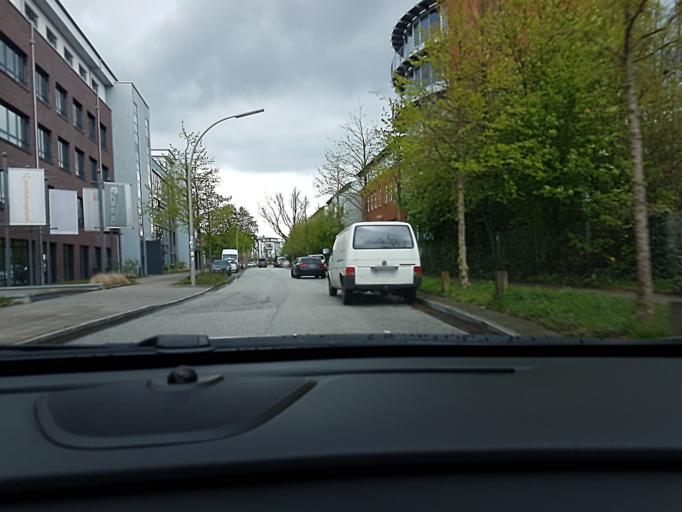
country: DE
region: Hamburg
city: Altona
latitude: 53.5571
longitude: 9.9101
